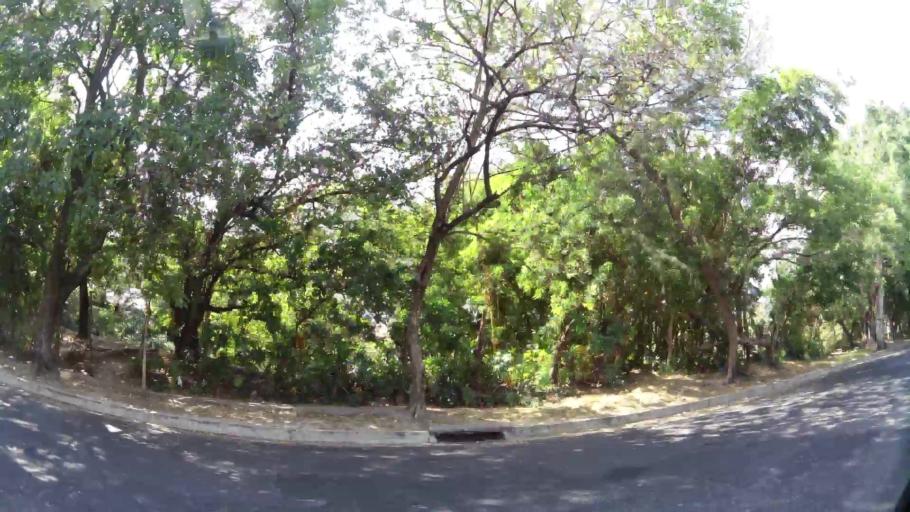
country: SV
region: San Salvador
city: Mejicanos
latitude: 13.7111
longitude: -89.2215
